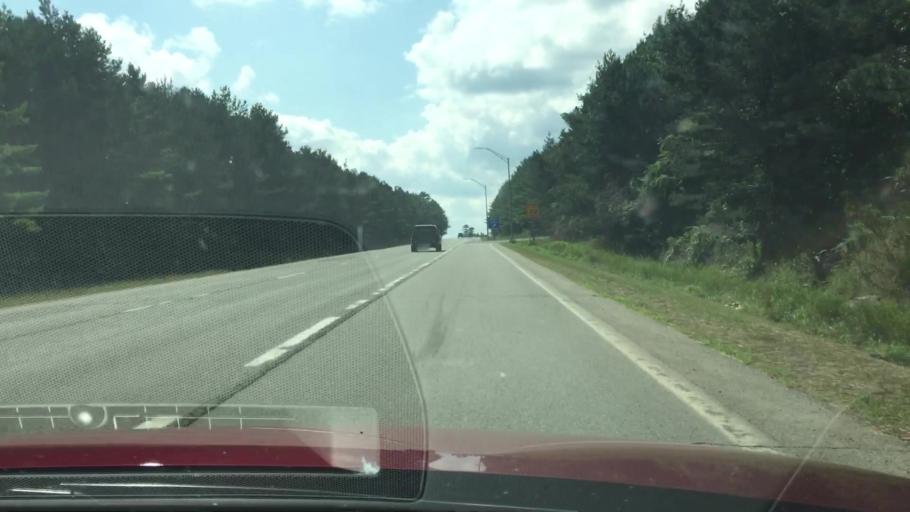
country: US
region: Maine
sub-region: Penobscot County
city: Medway
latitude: 45.5992
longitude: -68.5333
